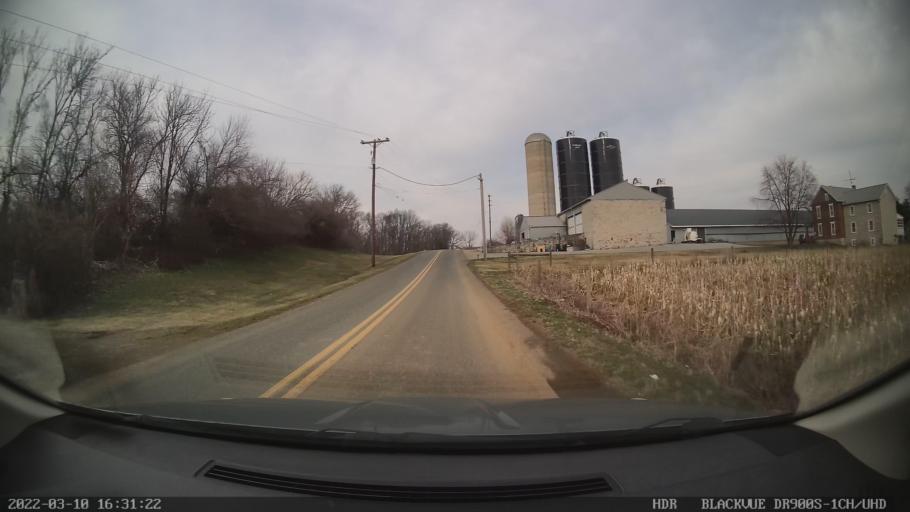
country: US
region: Pennsylvania
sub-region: Berks County
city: Oley
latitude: 40.3518
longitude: -75.7897
